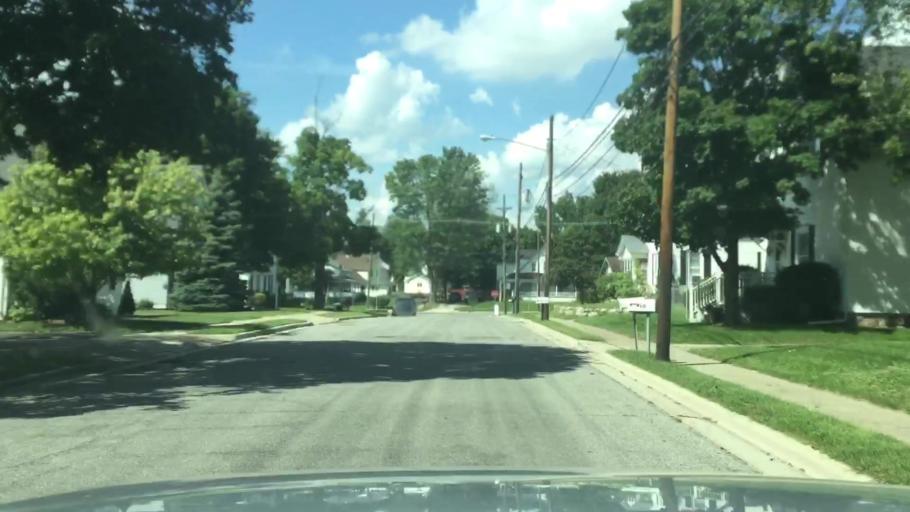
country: US
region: Michigan
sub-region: Lenawee County
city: Clinton
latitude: 42.0723
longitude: -83.9683
